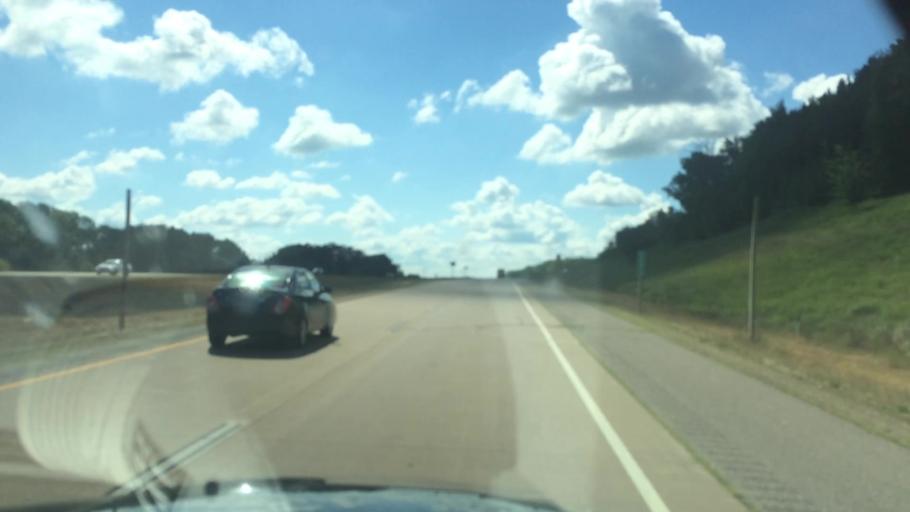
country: US
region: Wisconsin
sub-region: Portage County
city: Amherst
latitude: 44.4167
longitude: -89.2476
